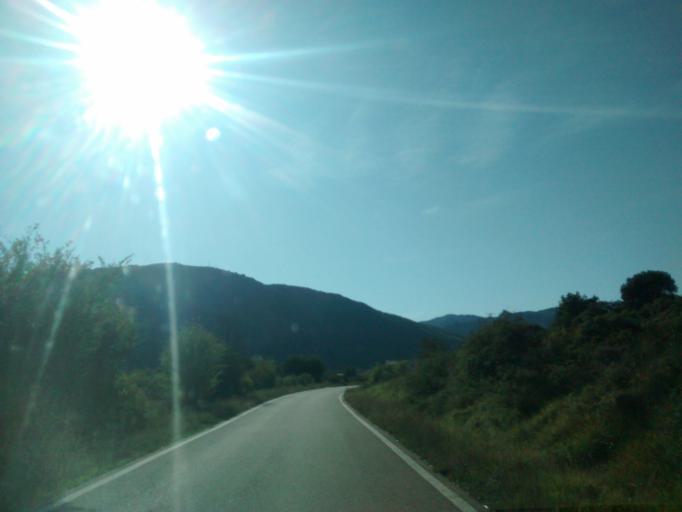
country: ES
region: Aragon
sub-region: Provincia de Huesca
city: Loarre
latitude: 42.3821
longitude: -0.6910
